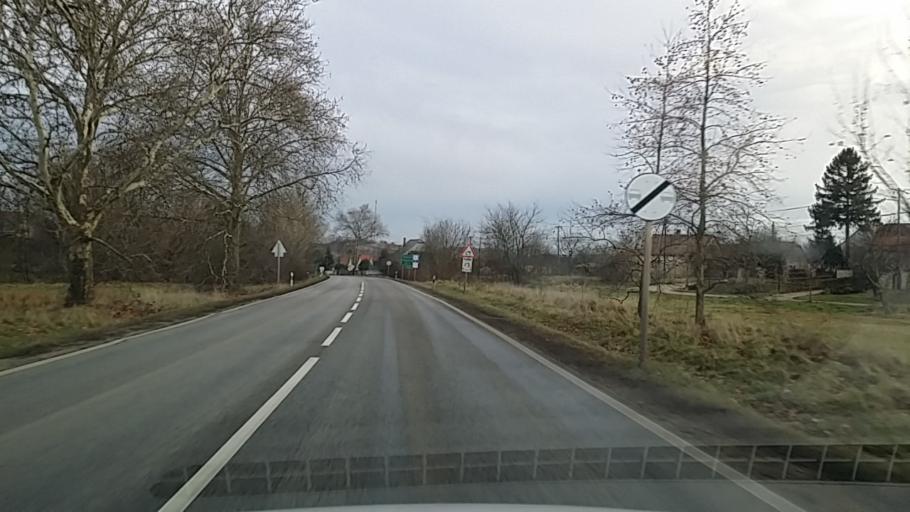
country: HU
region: Fejer
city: Mor
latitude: 47.3725
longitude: 18.1929
